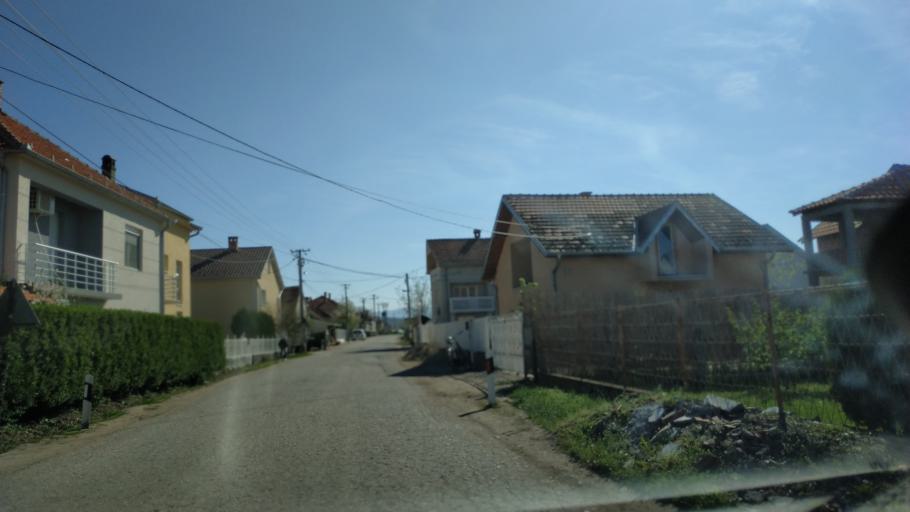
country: RS
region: Central Serbia
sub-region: Nisavski Okrug
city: Aleksinac
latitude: 43.5094
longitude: 21.6891
